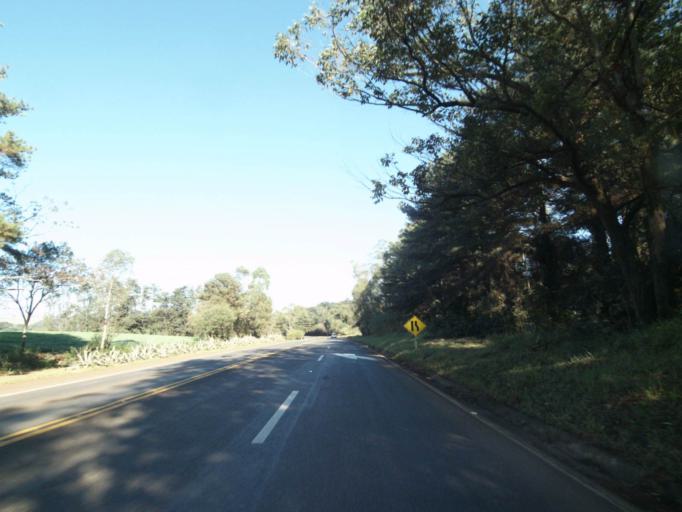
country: BR
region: Parana
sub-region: Faxinal
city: Faxinal
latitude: -23.7511
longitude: -51.1341
